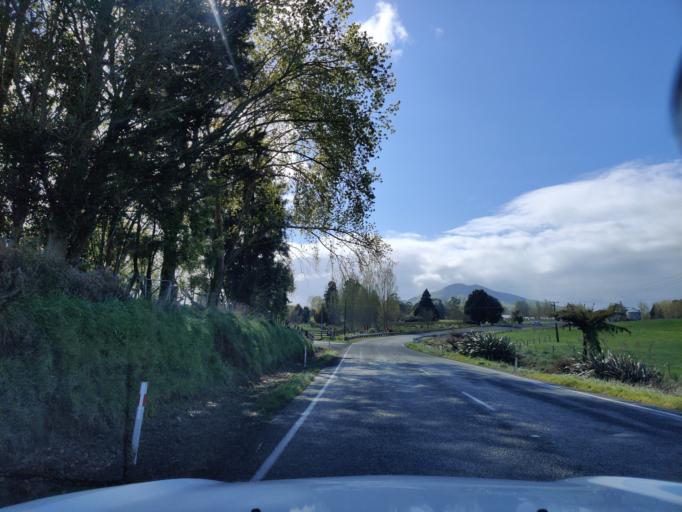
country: NZ
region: Waikato
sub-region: Otorohanga District
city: Otorohanga
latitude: -38.0681
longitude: 175.1720
